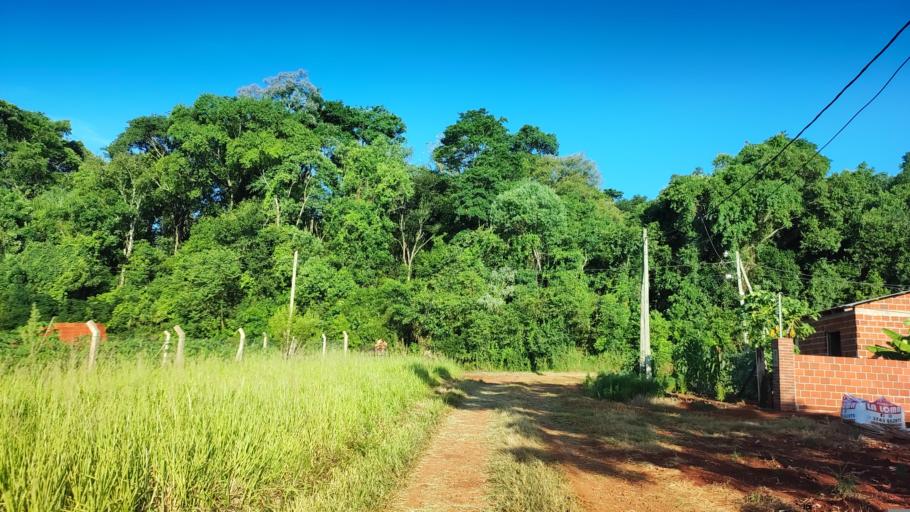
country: AR
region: Misiones
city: Capiovi
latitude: -26.9305
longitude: -55.0689
